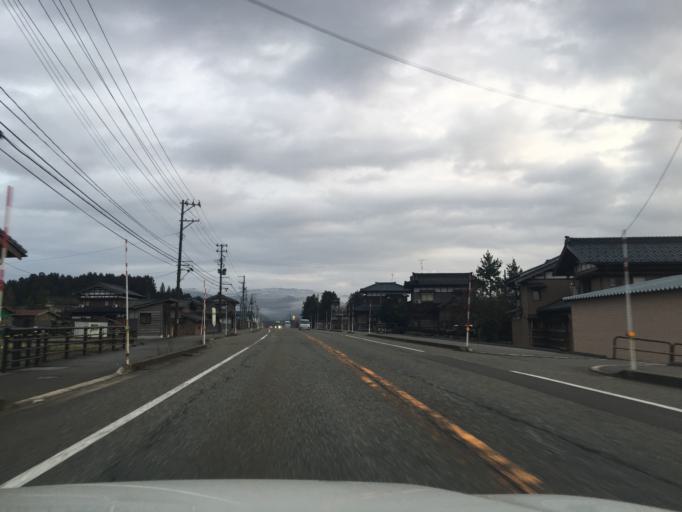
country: JP
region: Niigata
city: Murakami
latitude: 38.3139
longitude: 139.5486
